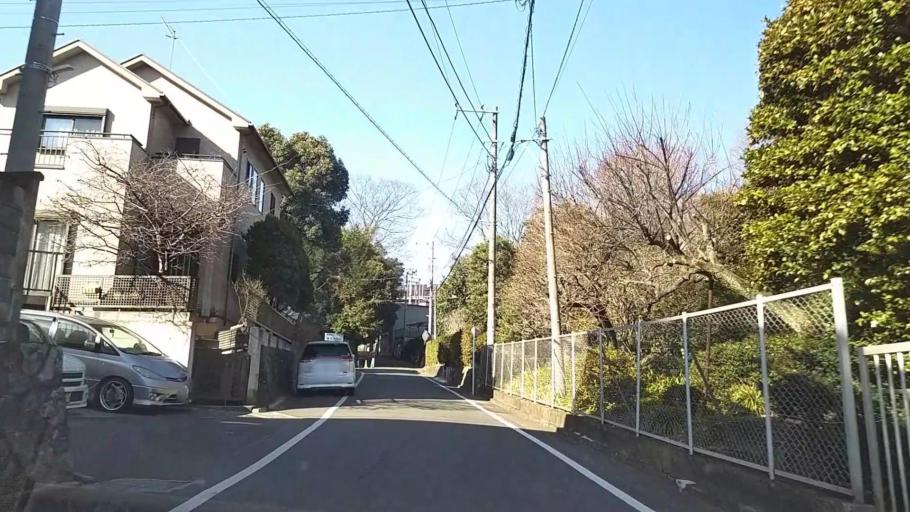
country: JP
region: Kanagawa
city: Hadano
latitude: 35.3795
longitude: 139.2218
